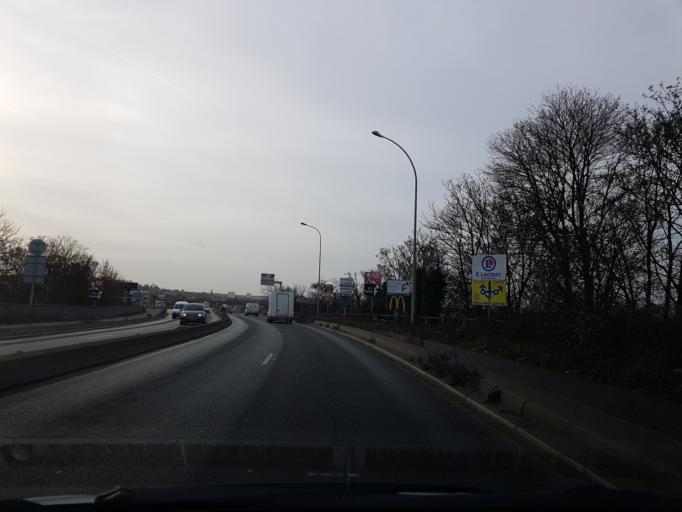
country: FR
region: Ile-de-France
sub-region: Departement du Val-de-Marne
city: Villeneuve-Saint-Georges
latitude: 48.7219
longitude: 2.4430
